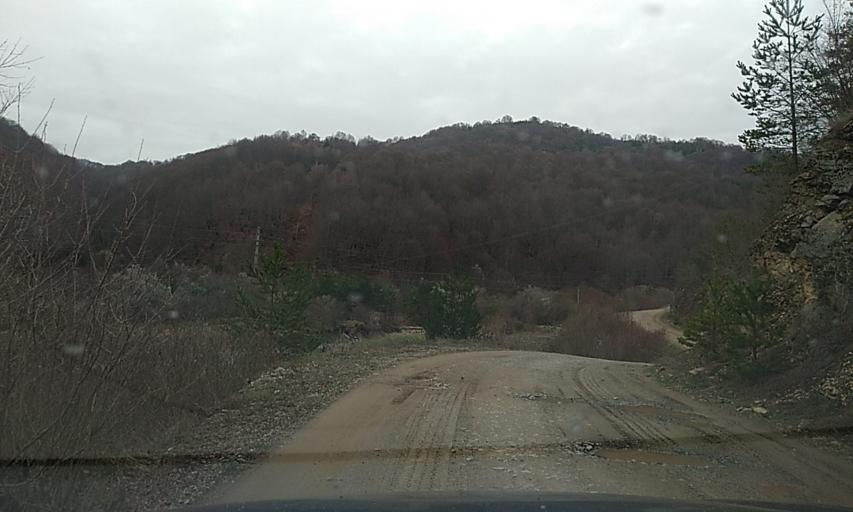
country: MK
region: Kriva Palanka
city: Kriva Palanka
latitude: 42.3421
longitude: 22.3922
